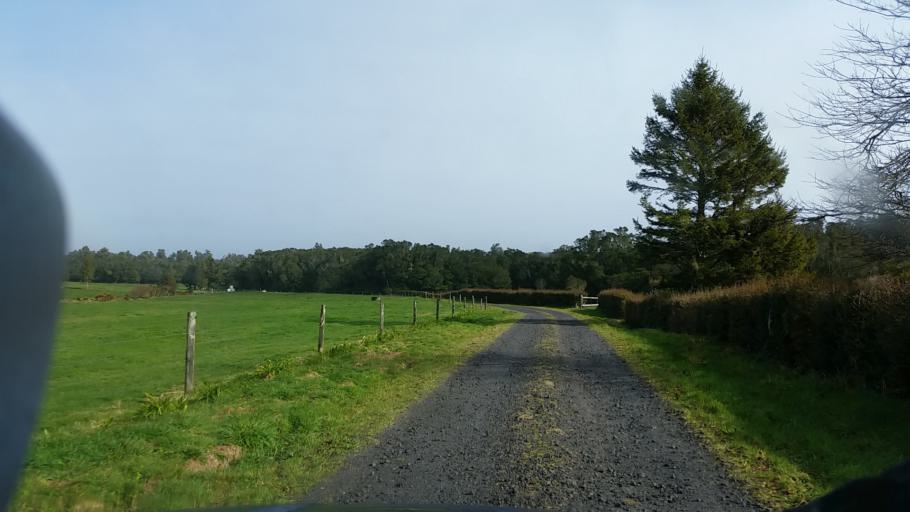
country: NZ
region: Taranaki
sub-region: South Taranaki District
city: Eltham
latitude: -39.2869
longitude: 174.1808
